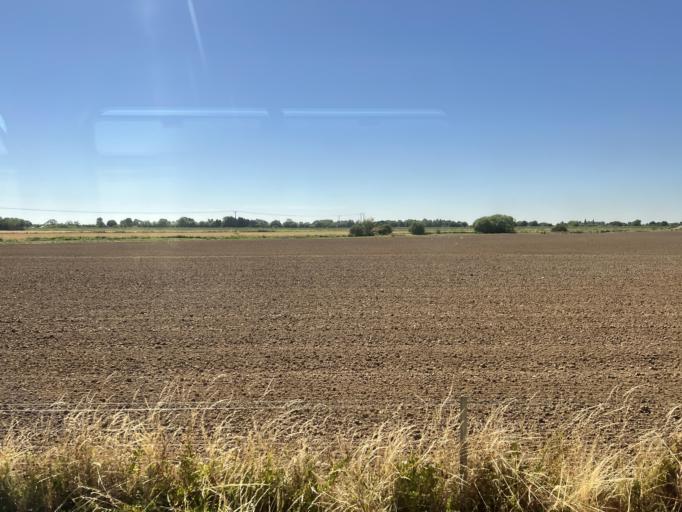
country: GB
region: England
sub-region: Lincolnshire
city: Wainfleet All Saints
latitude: 53.1159
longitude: 0.2114
